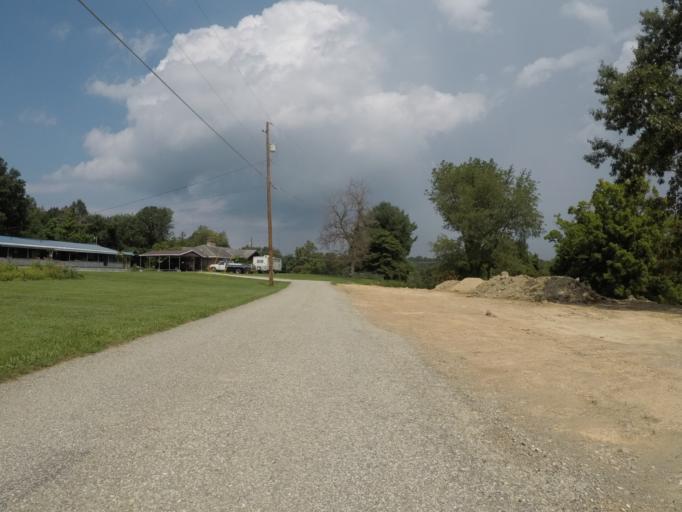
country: US
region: Kentucky
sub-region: Boyd County
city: Ironville
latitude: 38.4434
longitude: -82.7065
